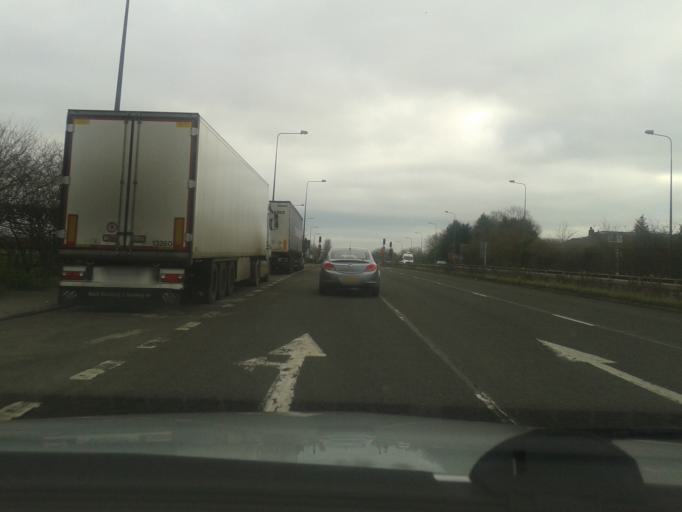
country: GB
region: England
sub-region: South Gloucestershire
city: Stoke Gifford
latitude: 51.5049
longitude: -2.5252
